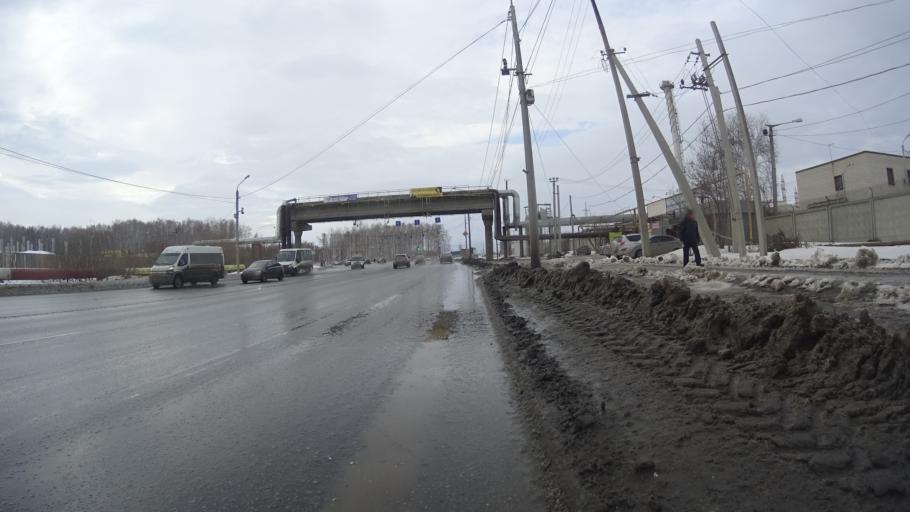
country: RU
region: Chelyabinsk
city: Roshchino
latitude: 55.2075
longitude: 61.3189
